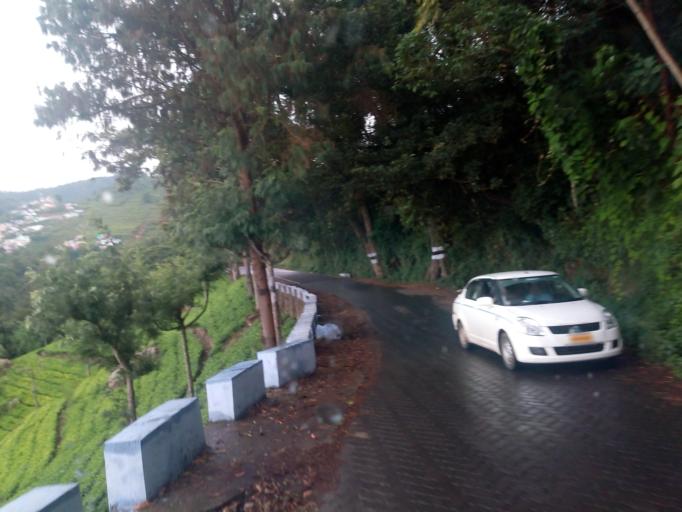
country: IN
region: Tamil Nadu
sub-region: Nilgiri
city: Wellington
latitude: 11.3616
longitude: 76.8407
